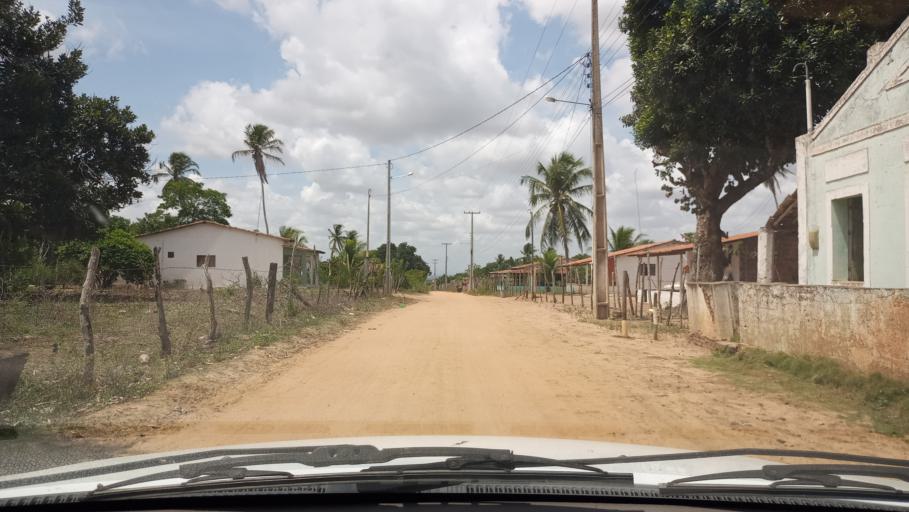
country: BR
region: Rio Grande do Norte
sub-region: Brejinho
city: Brejinho
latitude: -6.2609
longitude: -35.3410
